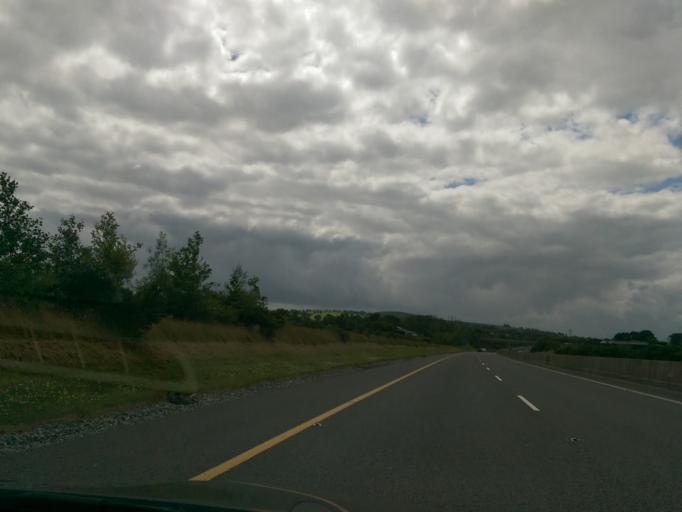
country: IE
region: Munster
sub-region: County Cork
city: Mitchelstown
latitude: 52.2601
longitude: -8.2505
